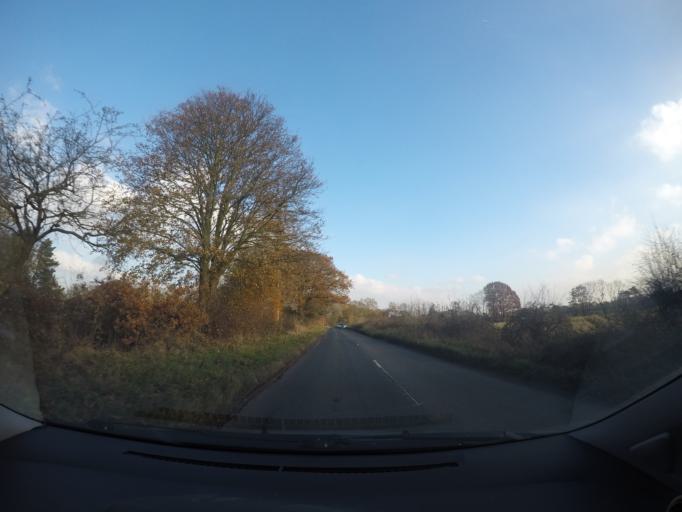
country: GB
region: England
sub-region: City of York
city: Huntington
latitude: 53.9991
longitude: -1.0399
